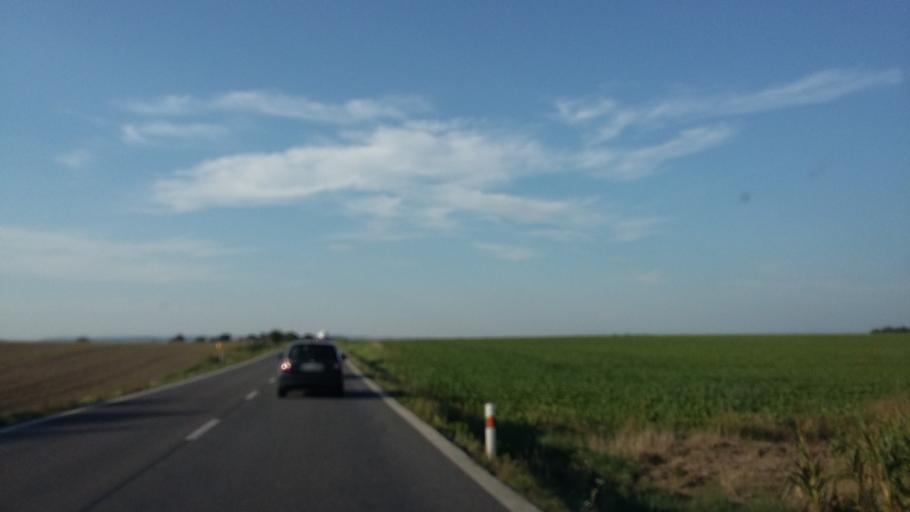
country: CZ
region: Central Bohemia
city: Lustenice
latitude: 50.2900
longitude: 14.9563
